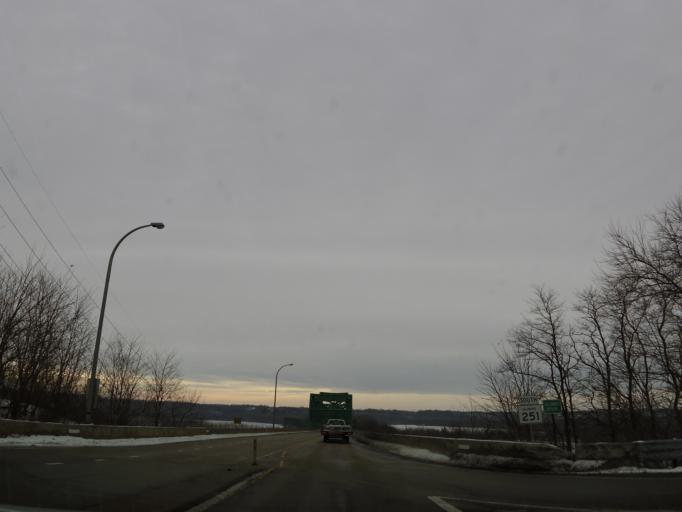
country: US
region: Illinois
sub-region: LaSalle County
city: Peru
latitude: 41.3265
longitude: -89.1200
